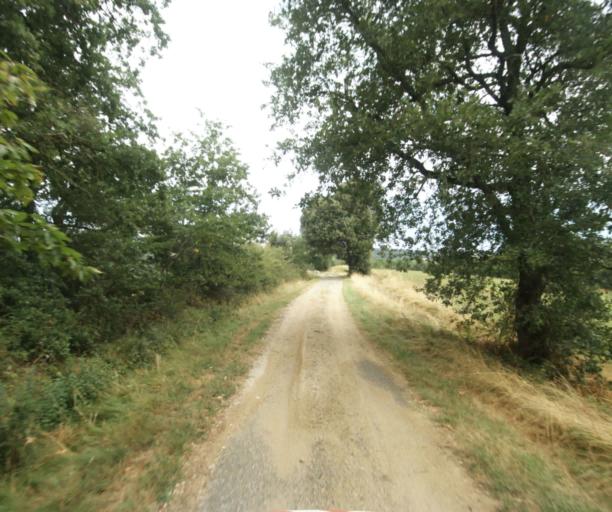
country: FR
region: Midi-Pyrenees
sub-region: Departement de la Haute-Garonne
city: Revel
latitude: 43.4141
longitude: 1.9819
